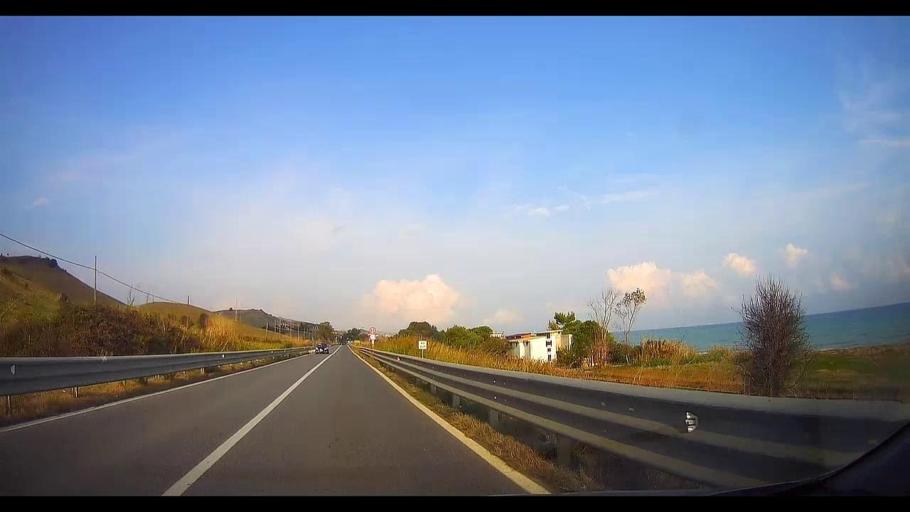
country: IT
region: Calabria
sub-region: Provincia di Cosenza
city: Cariati
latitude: 39.5149
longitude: 16.9171
